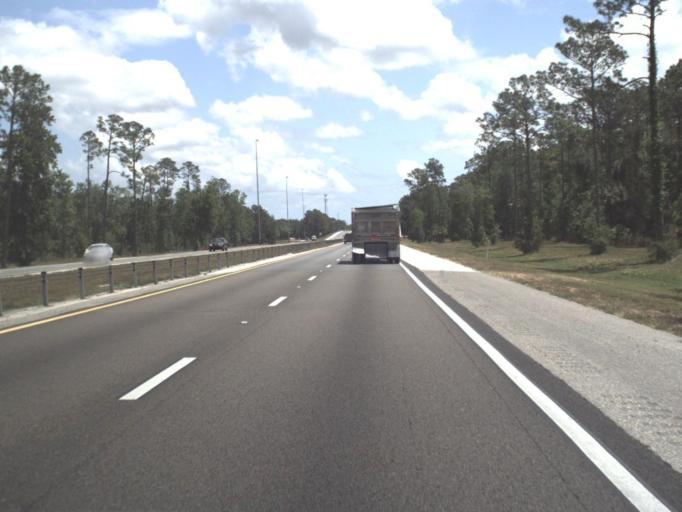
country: US
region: Florida
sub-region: Orange County
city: Christmas
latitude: 28.4524
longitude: -80.9884
